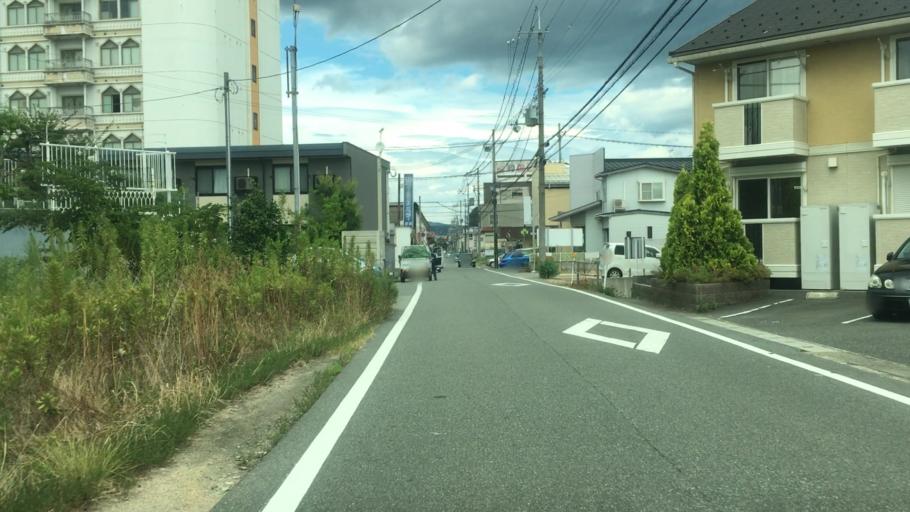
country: JP
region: Hyogo
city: Toyooka
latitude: 35.5325
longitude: 134.8209
